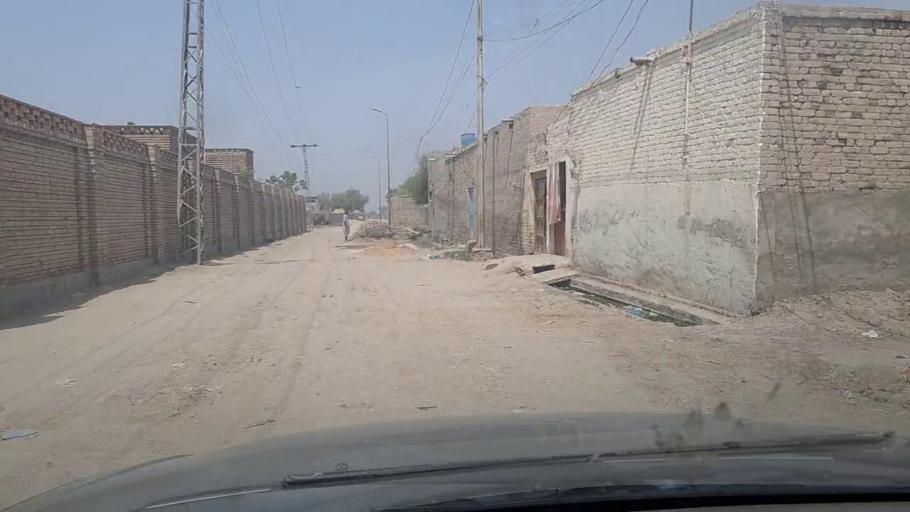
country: PK
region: Sindh
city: Adilpur
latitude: 27.9381
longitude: 69.3165
